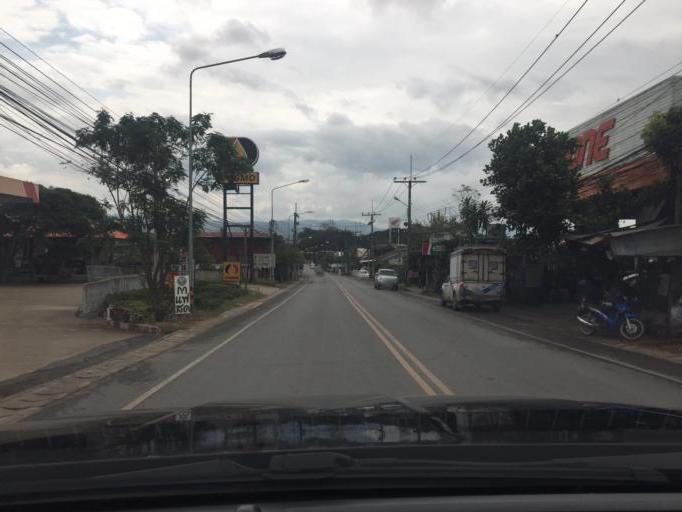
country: TH
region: Phayao
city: Pong
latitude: 19.1718
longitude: 100.2822
